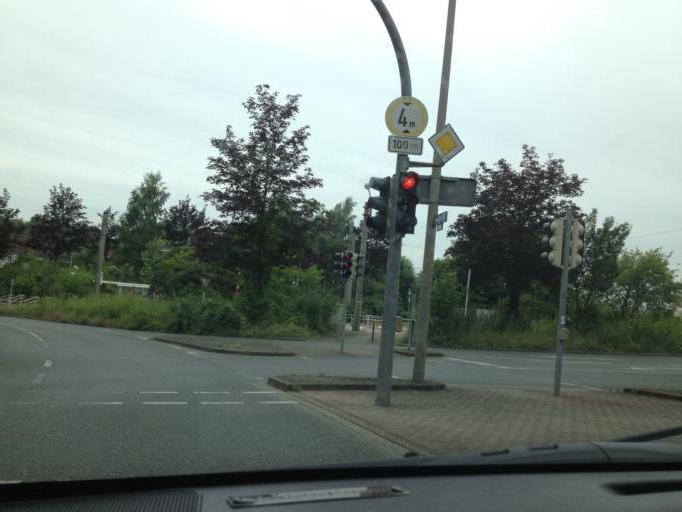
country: DE
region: North Rhine-Westphalia
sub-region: Regierungsbezirk Arnsberg
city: Dortmund
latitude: 51.5125
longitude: 7.4190
